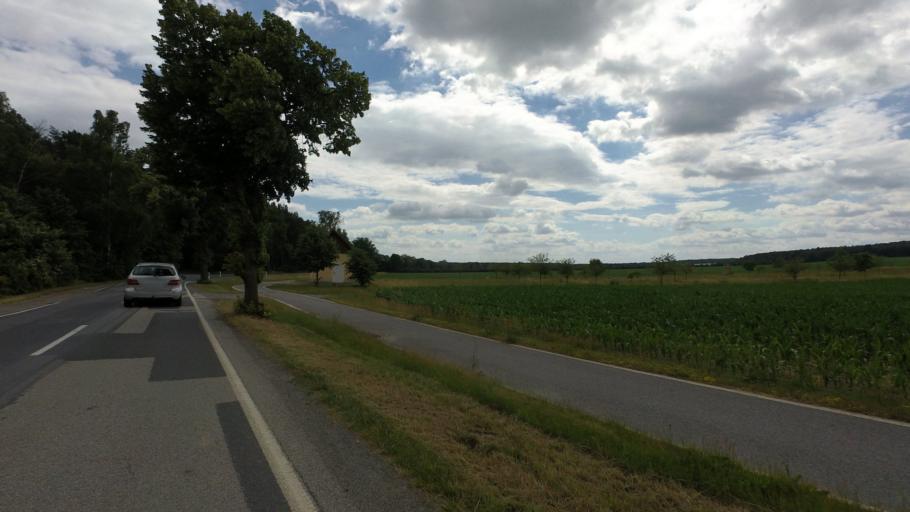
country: DE
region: Saxony
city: Ossling
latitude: 51.3561
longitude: 14.1663
